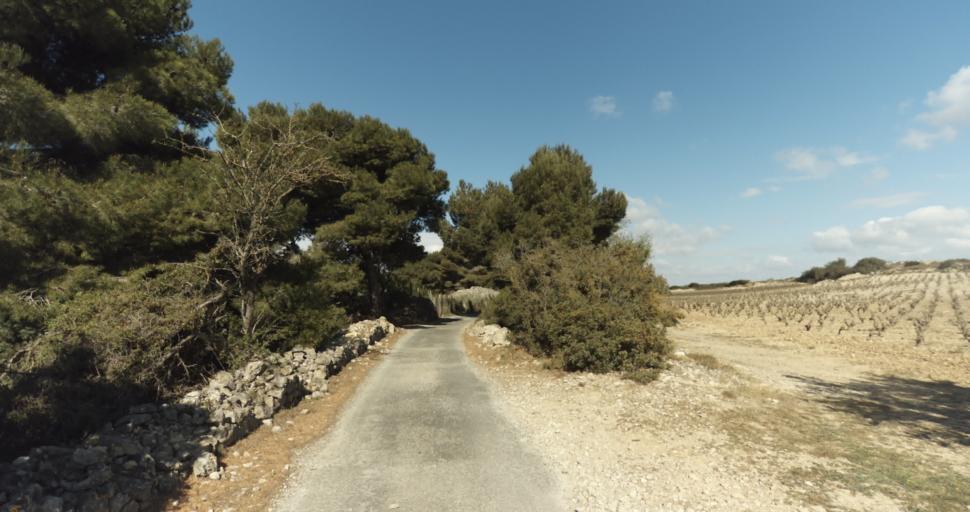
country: FR
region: Languedoc-Roussillon
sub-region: Departement de l'Aude
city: Leucate
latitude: 42.9189
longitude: 3.0304
